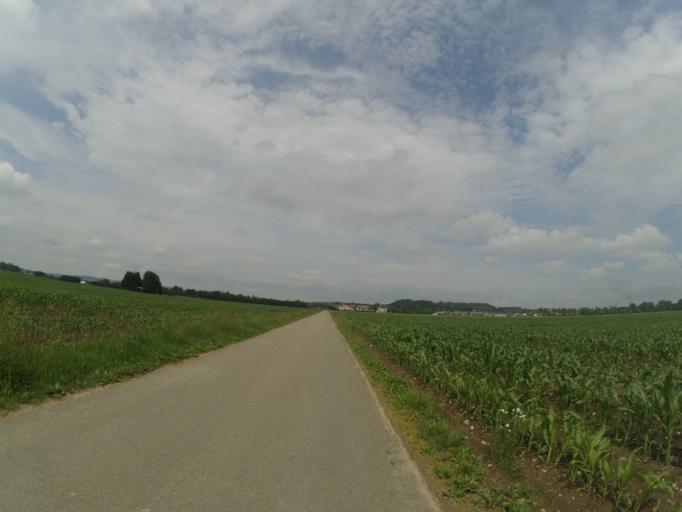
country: DE
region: Baden-Wuerttemberg
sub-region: Tuebingen Region
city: Leutkirch im Allgau
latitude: 47.8119
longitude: 10.0201
